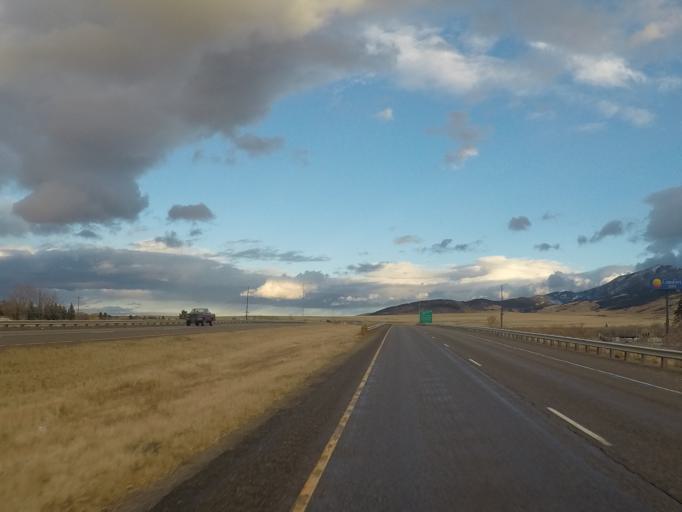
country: US
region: Montana
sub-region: Park County
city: Livingston
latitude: 45.6443
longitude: -110.5764
